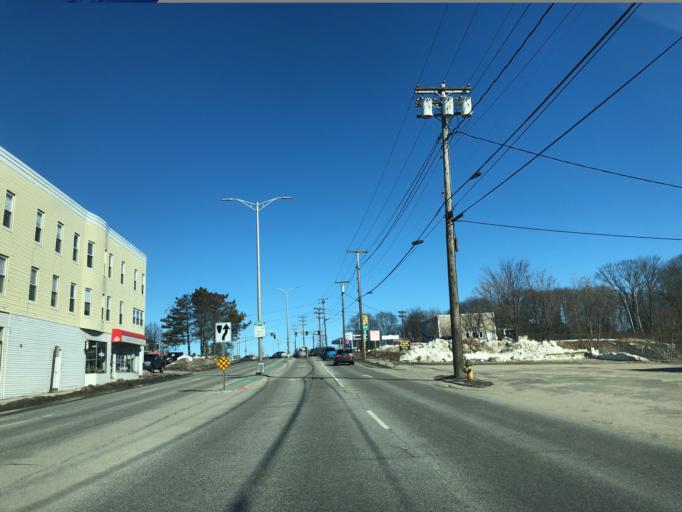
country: US
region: Maine
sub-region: Androscoggin County
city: Auburn
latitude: 44.1010
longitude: -70.2269
